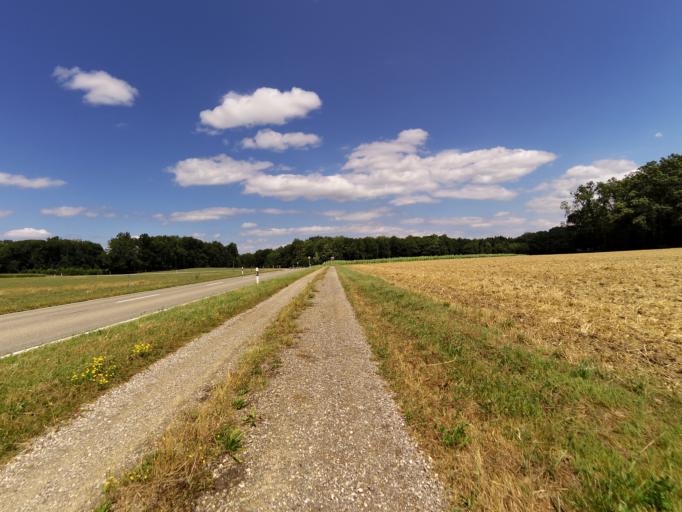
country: CH
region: Thurgau
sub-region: Kreuzlingen District
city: Tagerwilen
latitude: 47.6340
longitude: 9.1007
